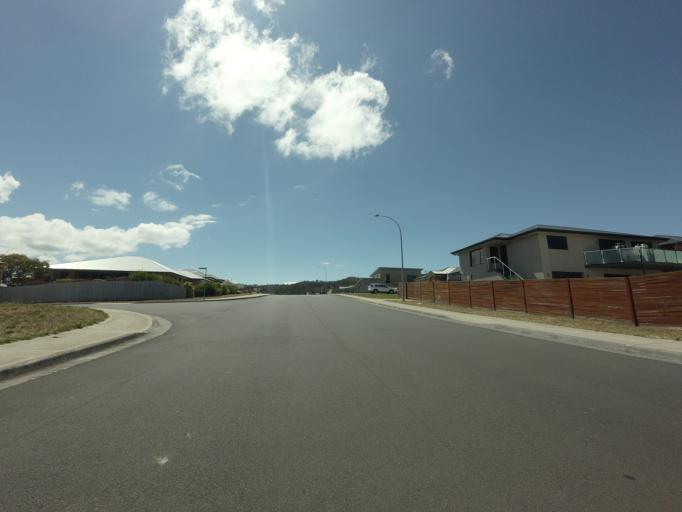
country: AU
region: Tasmania
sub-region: Clarence
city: Rokeby
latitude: -42.9003
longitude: 147.4521
